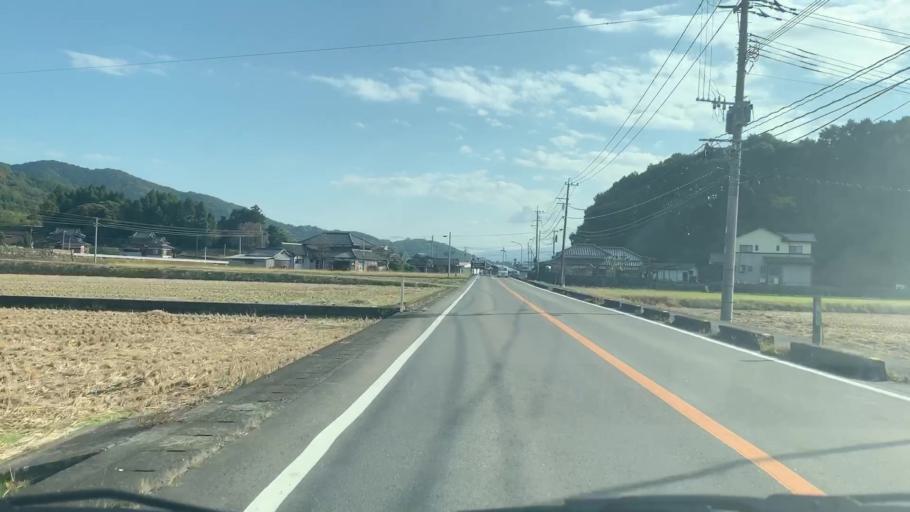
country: JP
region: Saga Prefecture
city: Kashima
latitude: 33.1534
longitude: 130.0643
